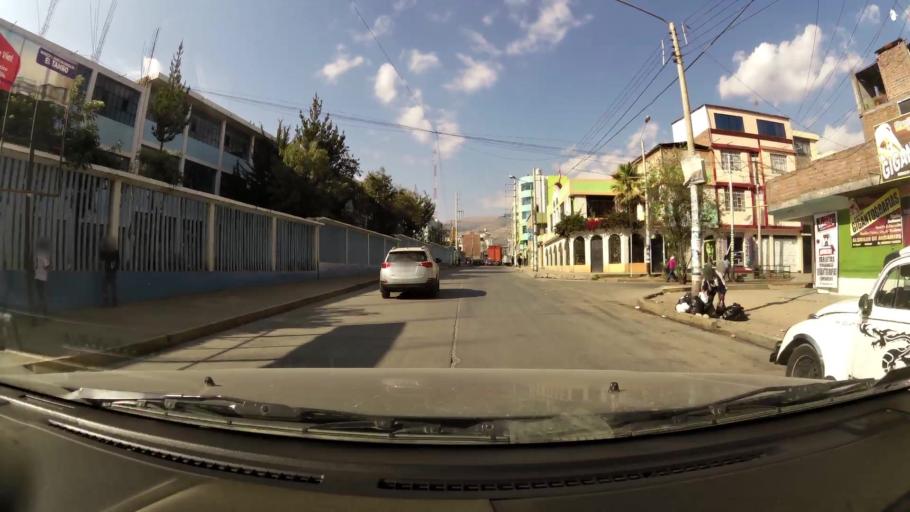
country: PE
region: Junin
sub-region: Provincia de Huancayo
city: El Tambo
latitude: -12.0628
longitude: -75.2164
